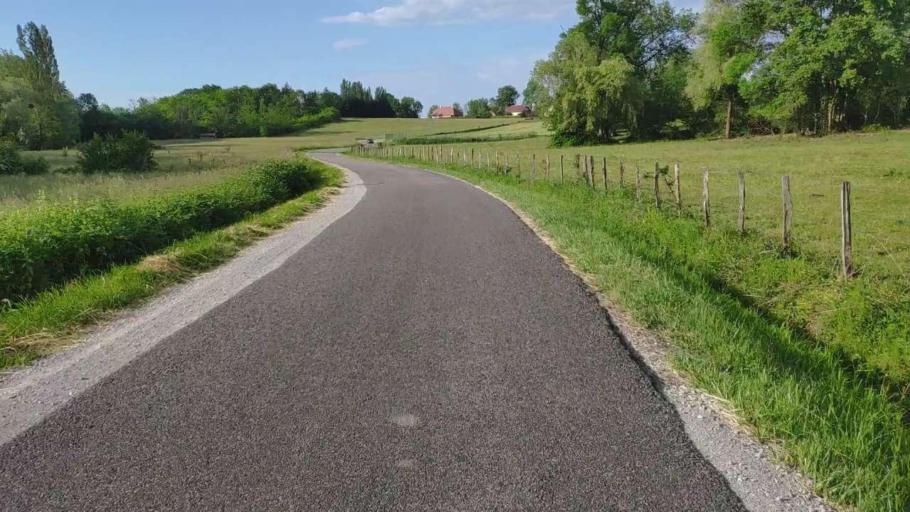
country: FR
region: Franche-Comte
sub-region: Departement du Jura
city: Bletterans
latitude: 46.7534
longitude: 5.4489
